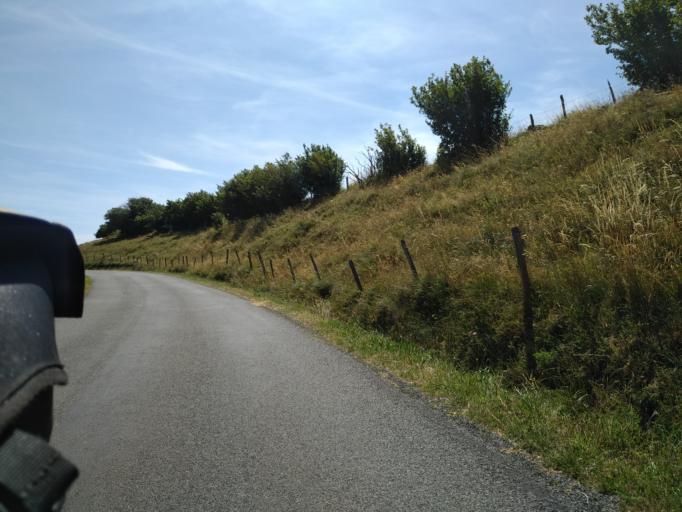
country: FR
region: Auvergne
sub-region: Departement du Cantal
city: Chaudes-Aigues
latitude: 44.6504
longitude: 3.0655
